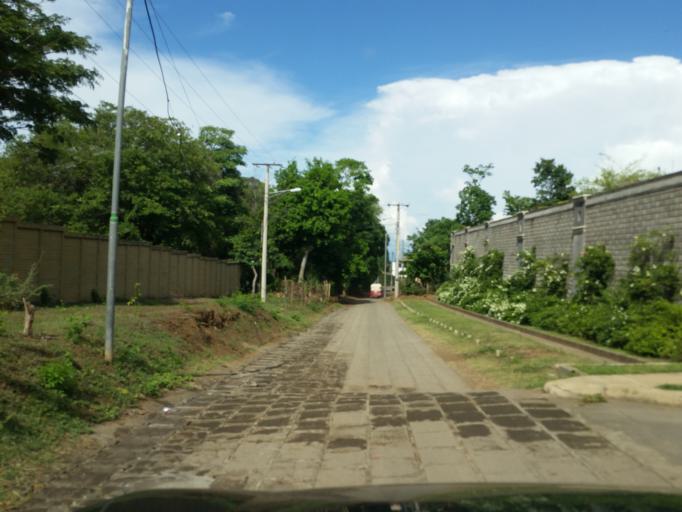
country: NI
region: Managua
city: Managua
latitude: 12.0738
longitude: -86.2410
